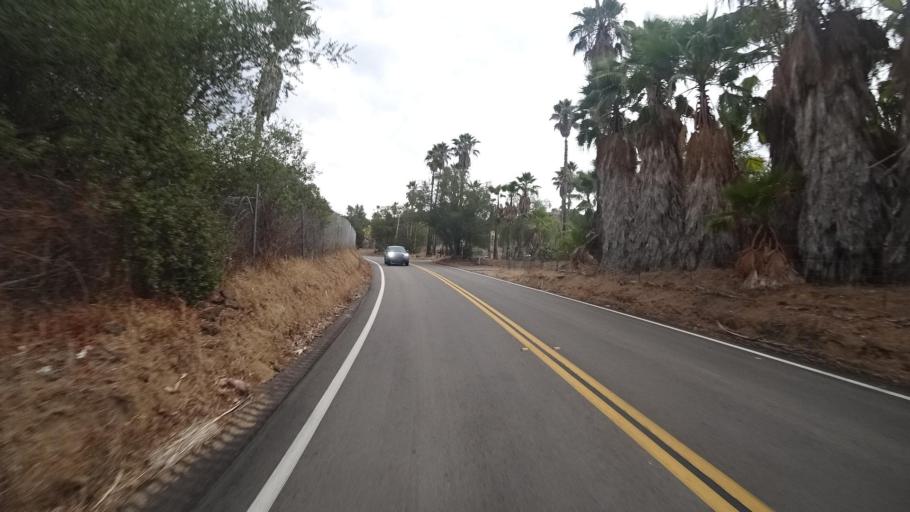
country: US
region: California
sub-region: San Diego County
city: San Pasqual
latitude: 33.0580
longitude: -116.9732
